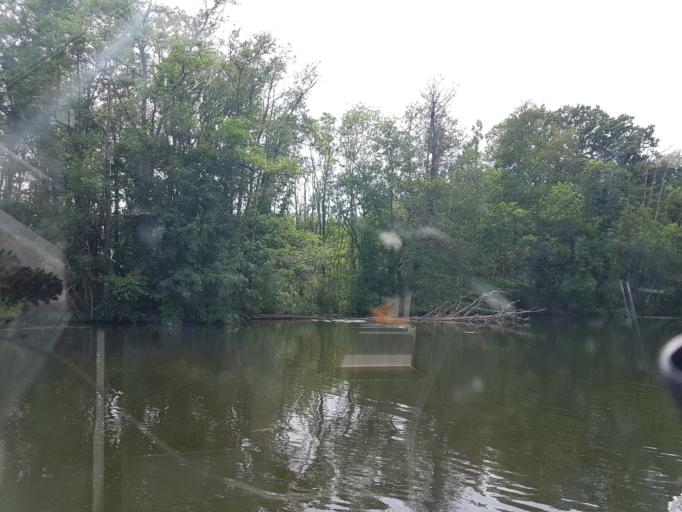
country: FR
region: Bourgogne
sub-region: Departement de l'Yonne
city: Gurgy
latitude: 47.8594
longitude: 3.5545
